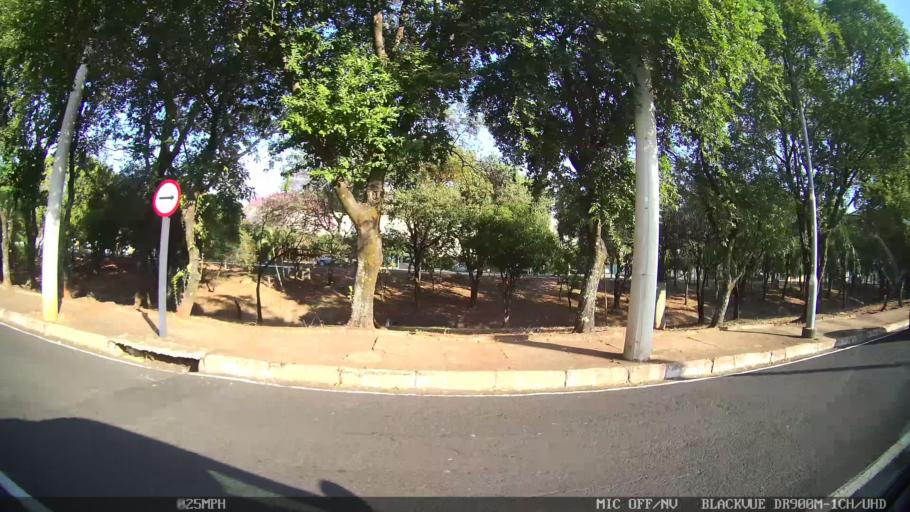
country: BR
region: Sao Paulo
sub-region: Sao Jose Do Rio Preto
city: Sao Jose do Rio Preto
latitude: -20.8240
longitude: -49.3656
